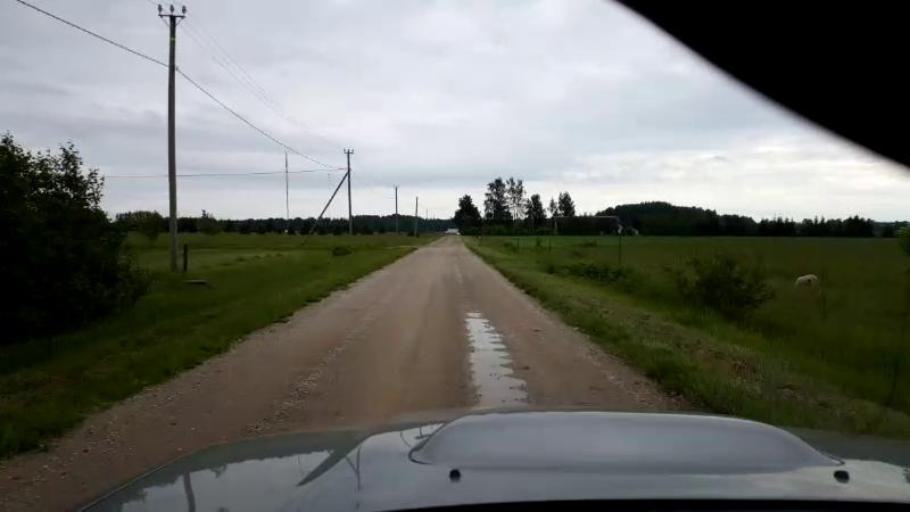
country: EE
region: Paernumaa
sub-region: Halinga vald
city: Parnu-Jaagupi
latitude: 58.5364
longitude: 24.5754
